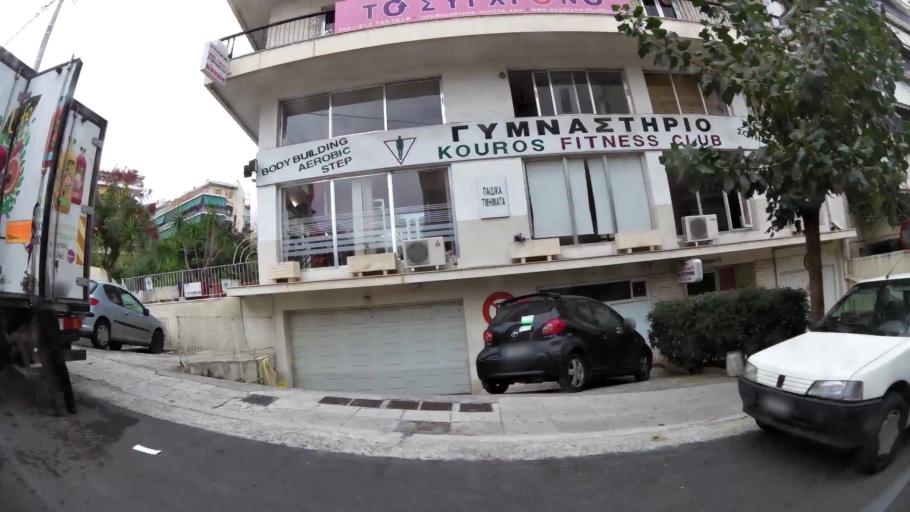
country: GR
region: Attica
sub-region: Nomarchia Athinas
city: Vyronas
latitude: 37.9624
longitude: 23.7556
